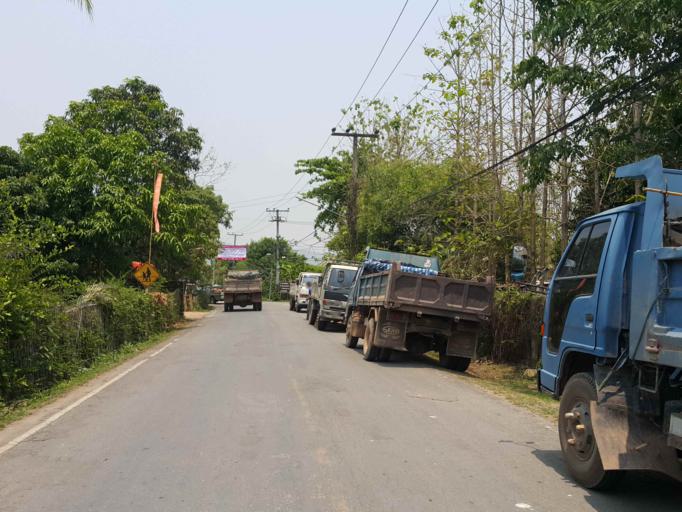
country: TH
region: Chiang Mai
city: San Sai
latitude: 18.8953
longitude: 99.0834
